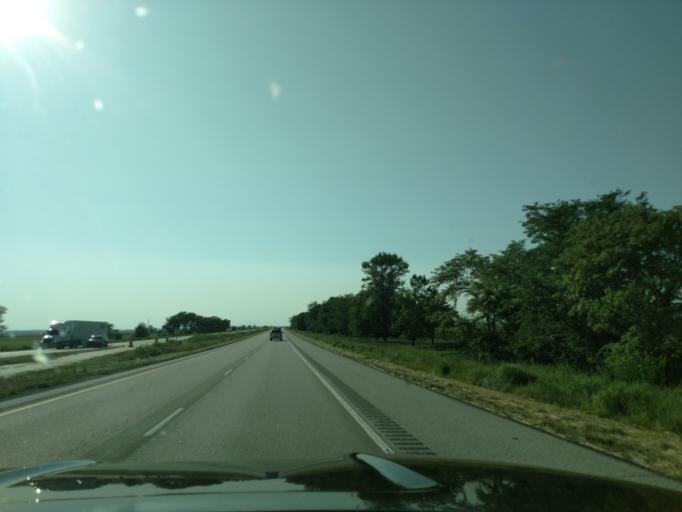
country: US
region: Iowa
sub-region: Fremont County
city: Hamburg
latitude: 40.5895
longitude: -95.6621
